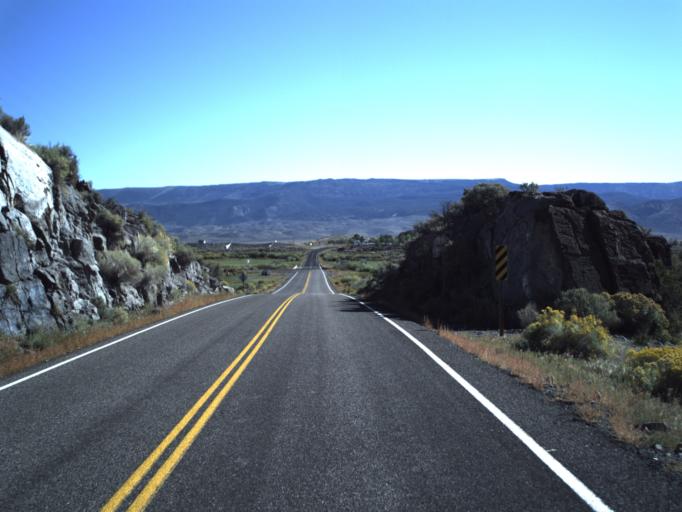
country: US
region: Utah
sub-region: Piute County
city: Junction
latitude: 38.1652
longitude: -112.0298
